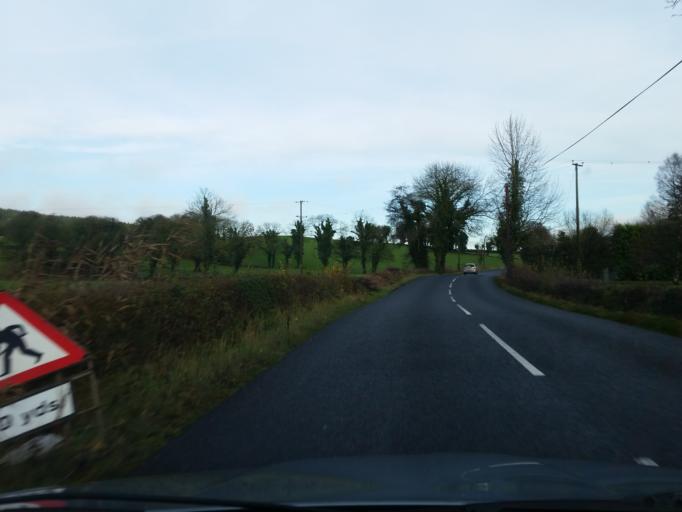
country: IE
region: Ulster
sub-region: County Monaghan
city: Clones
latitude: 54.2259
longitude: -7.3226
